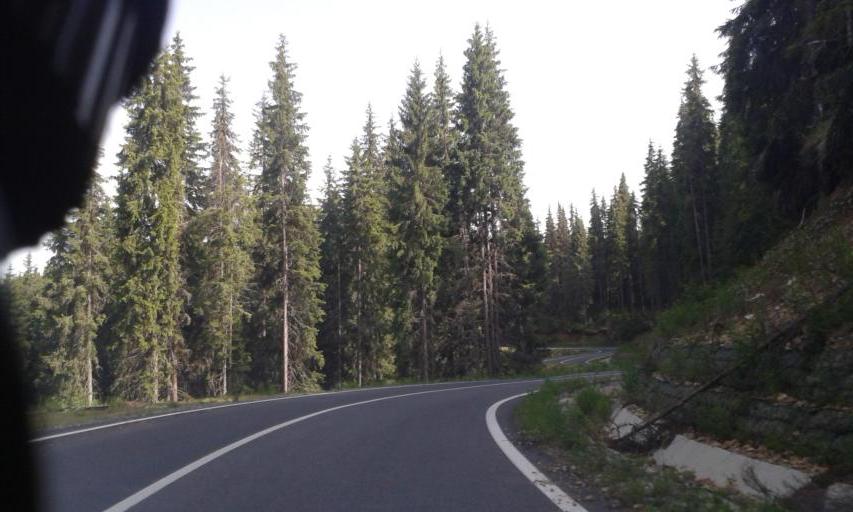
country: RO
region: Hunedoara
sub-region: Oras Petrila
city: Petrila
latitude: 45.5010
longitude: 23.6393
